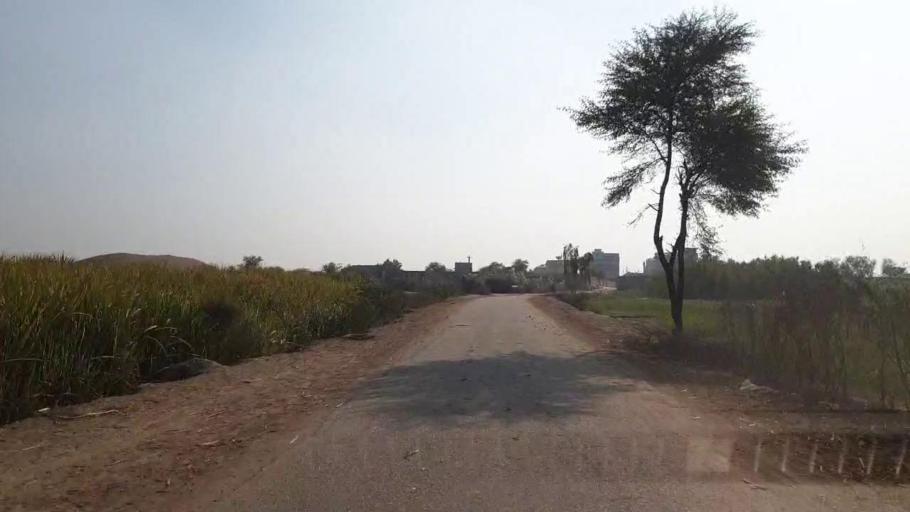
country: PK
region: Sindh
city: Tando Adam
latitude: 25.6616
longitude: 68.5764
